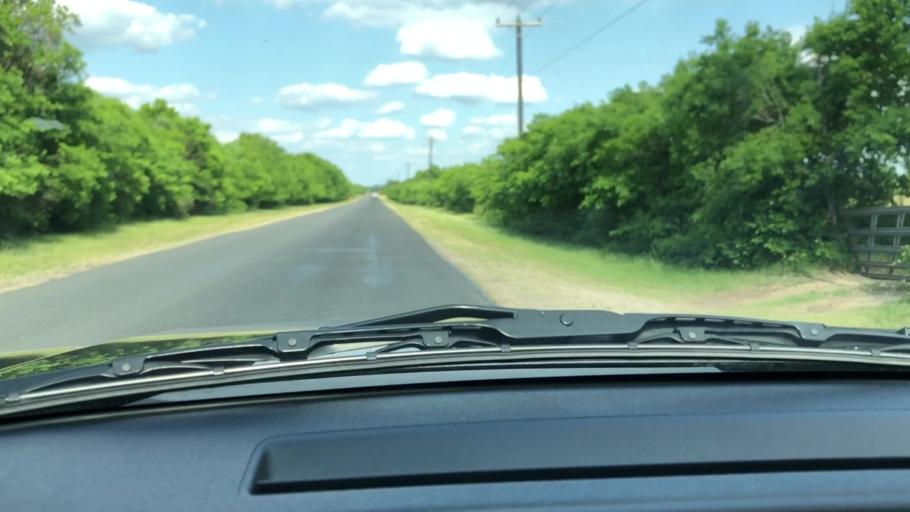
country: US
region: Texas
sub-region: Bexar County
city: Timberwood Park
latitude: 29.7307
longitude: -98.5102
